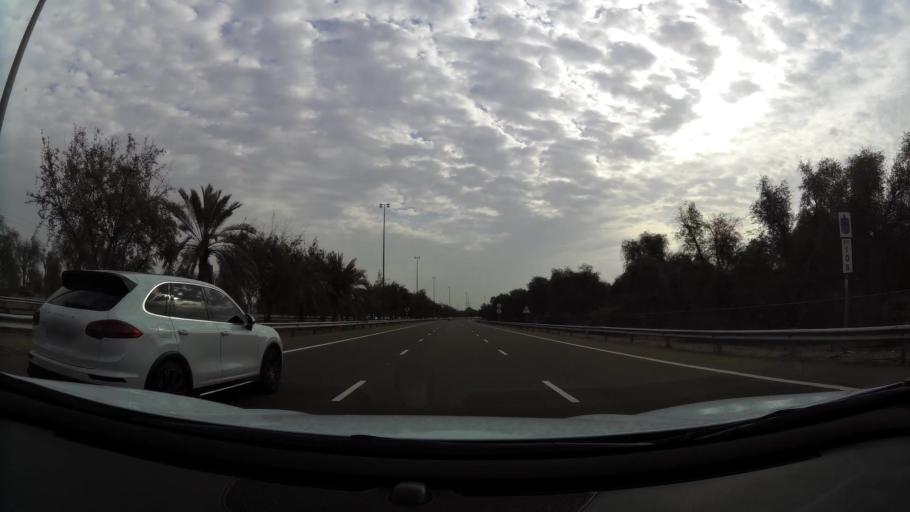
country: AE
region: Abu Dhabi
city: Al Ain
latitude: 24.1687
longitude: 55.2614
